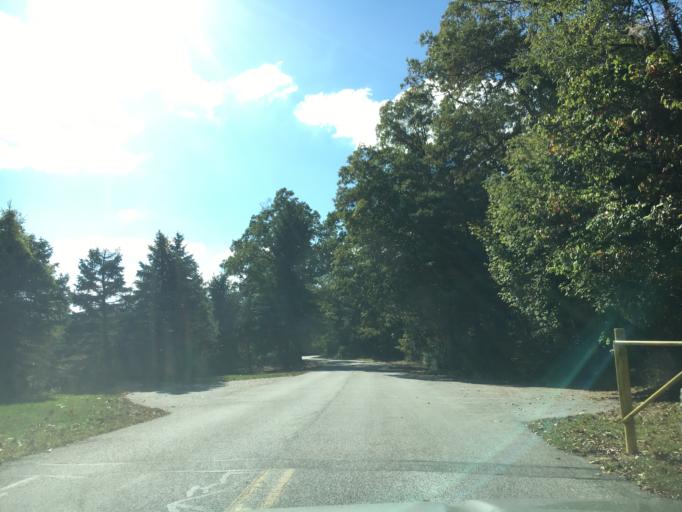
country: US
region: Pennsylvania
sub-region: York County
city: Yorklyn
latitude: 40.0080
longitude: -76.6656
